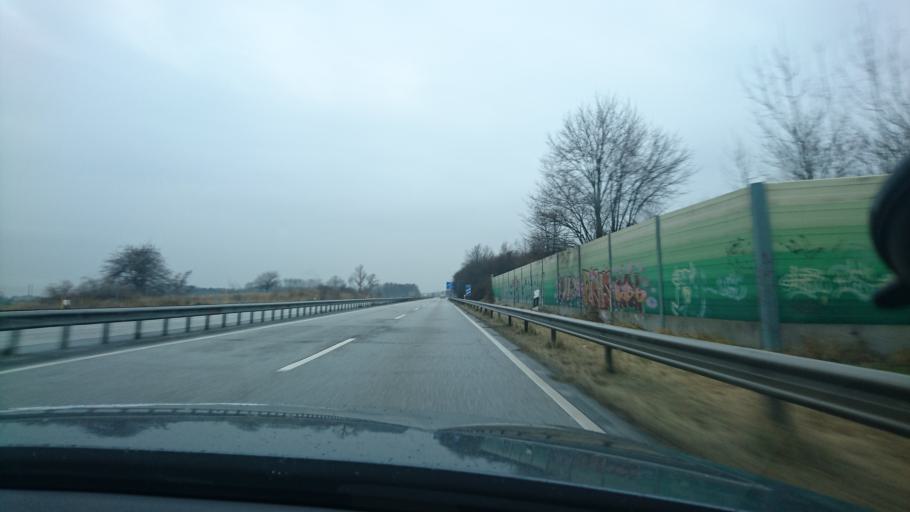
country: DE
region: Schleswig-Holstein
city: Oldenburg in Holstein
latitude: 54.2802
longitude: 10.8801
